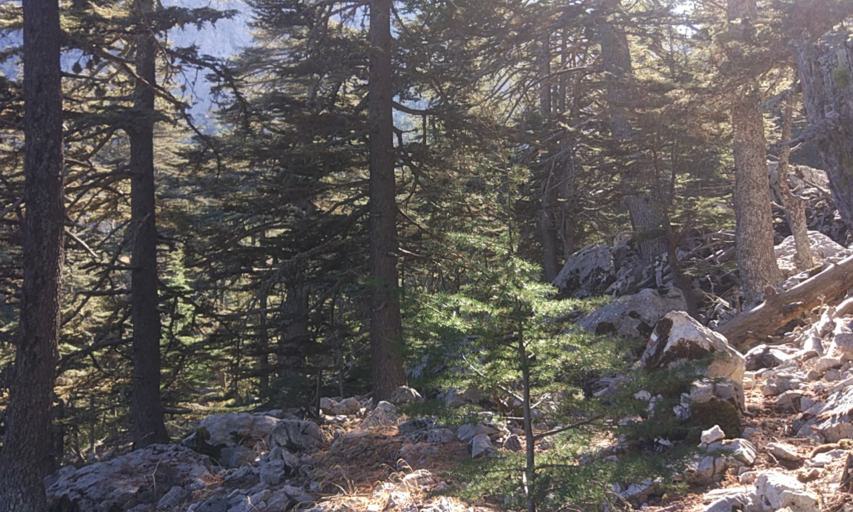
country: TR
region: Antalya
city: Altinyaka
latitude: 36.5563
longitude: 30.4158
